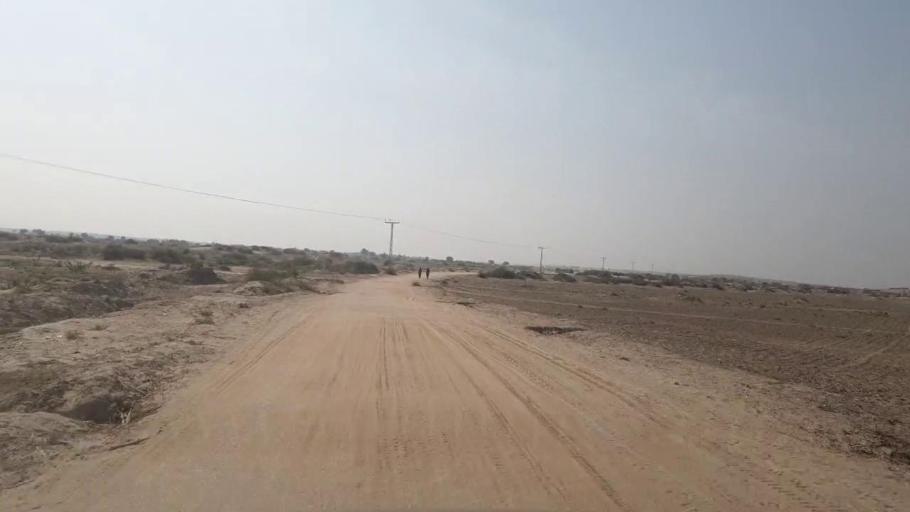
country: PK
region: Sindh
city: Umarkot
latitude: 25.3207
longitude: 69.7301
